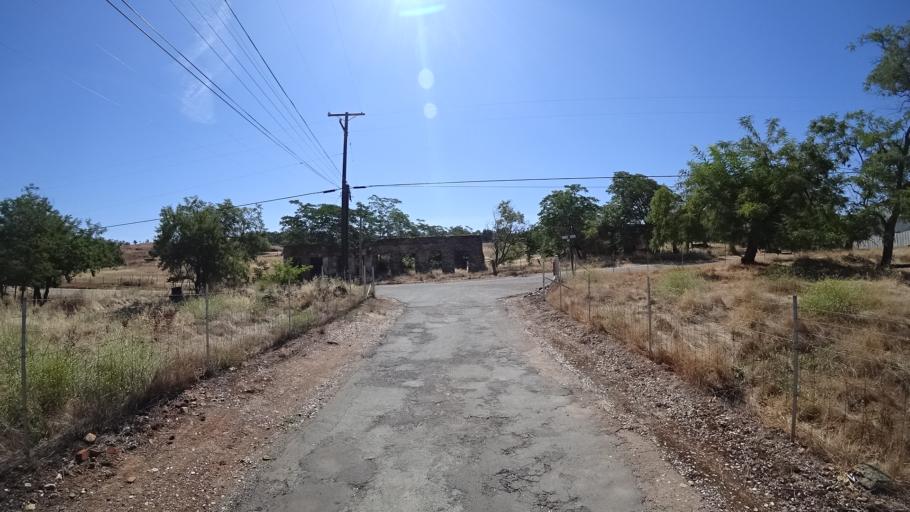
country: US
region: California
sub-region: Calaveras County
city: Valley Springs
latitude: 38.2268
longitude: -120.8544
